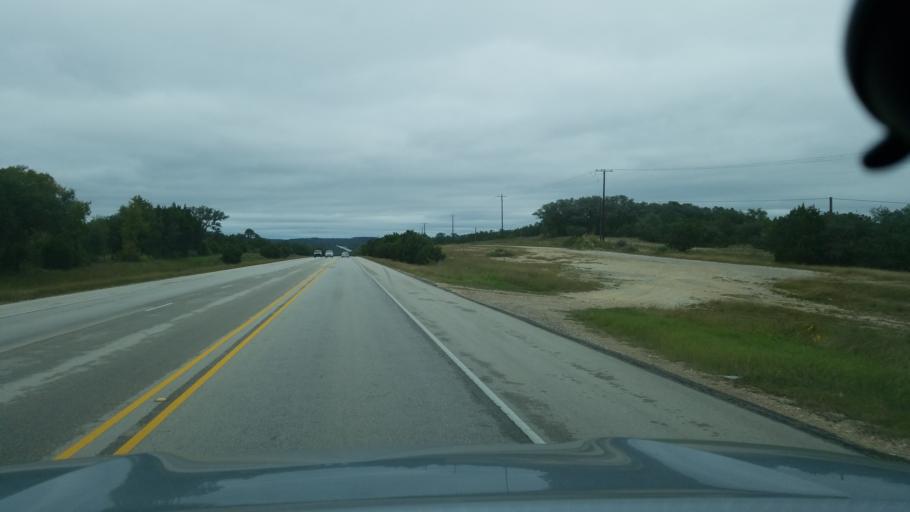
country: US
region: Texas
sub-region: Blanco County
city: Blanco
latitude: 29.9828
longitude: -98.4089
